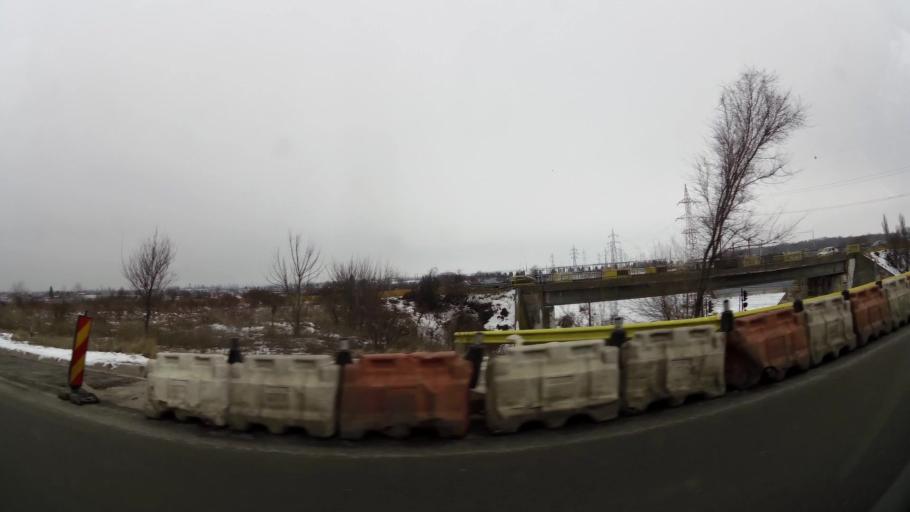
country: RO
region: Ilfov
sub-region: Comuna Chitila
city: Chitila
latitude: 44.5203
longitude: 25.9689
